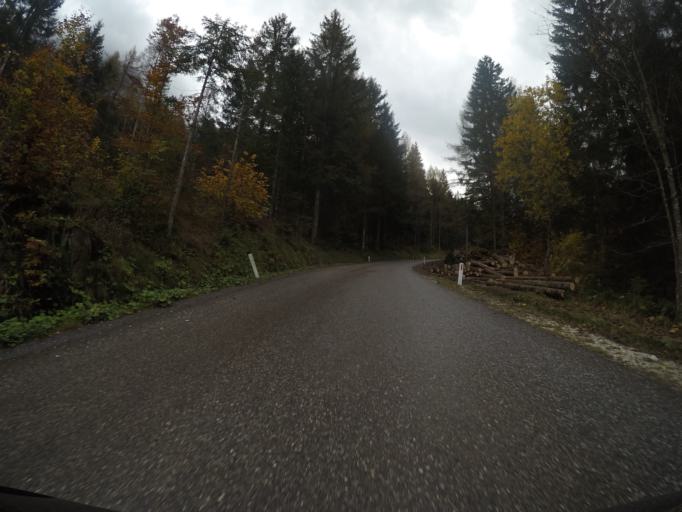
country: SI
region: Kranjska Gora
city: Mojstrana
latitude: 46.4505
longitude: 13.9355
